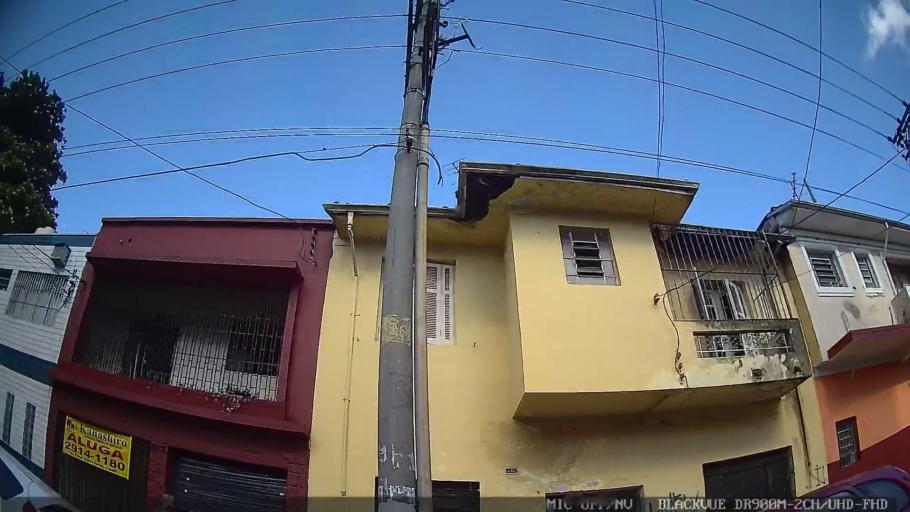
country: BR
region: Sao Paulo
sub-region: Sao Caetano Do Sul
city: Sao Caetano do Sul
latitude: -23.5988
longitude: -46.5993
